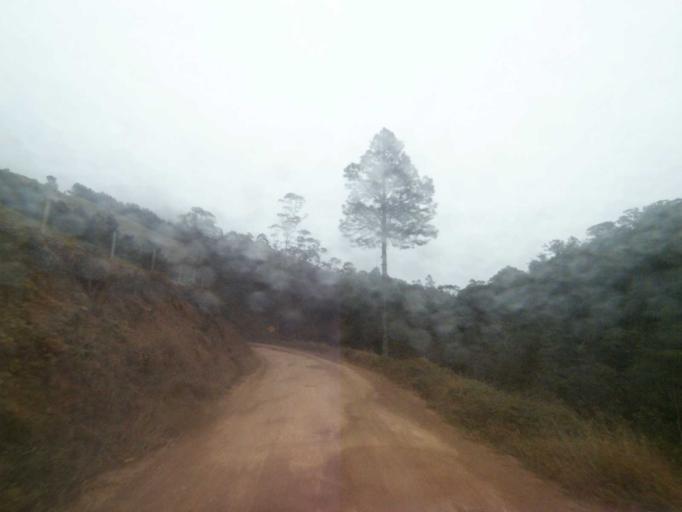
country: BR
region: Santa Catarina
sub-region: Anitapolis
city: Anitapolis
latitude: -27.8881
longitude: -49.1319
